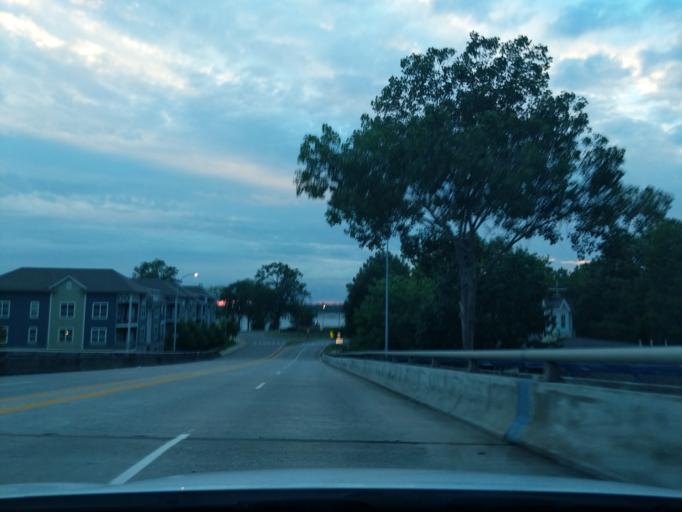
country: US
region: Tennessee
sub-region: Shelby County
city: Memphis
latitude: 35.1588
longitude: -90.0541
